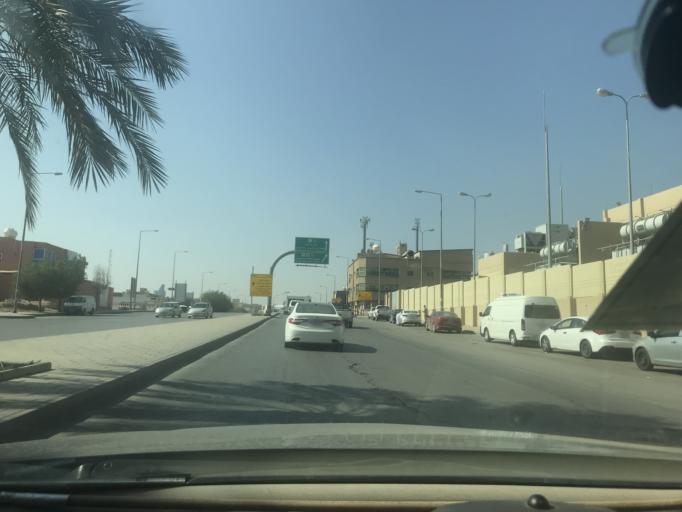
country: SA
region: Ar Riyad
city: Riyadh
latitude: 24.6668
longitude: 46.7217
